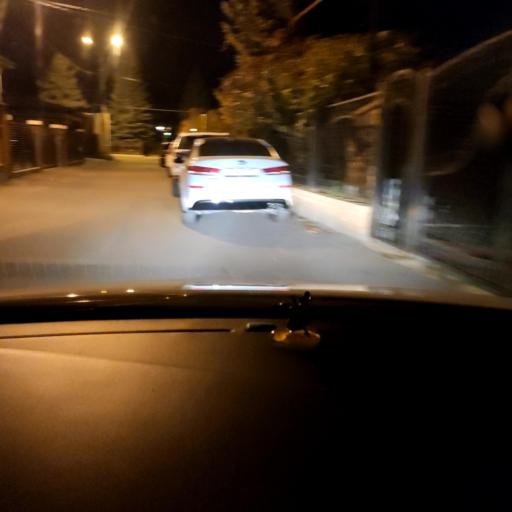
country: RU
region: Tatarstan
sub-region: Gorod Kazan'
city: Kazan
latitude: 55.7962
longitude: 49.0659
